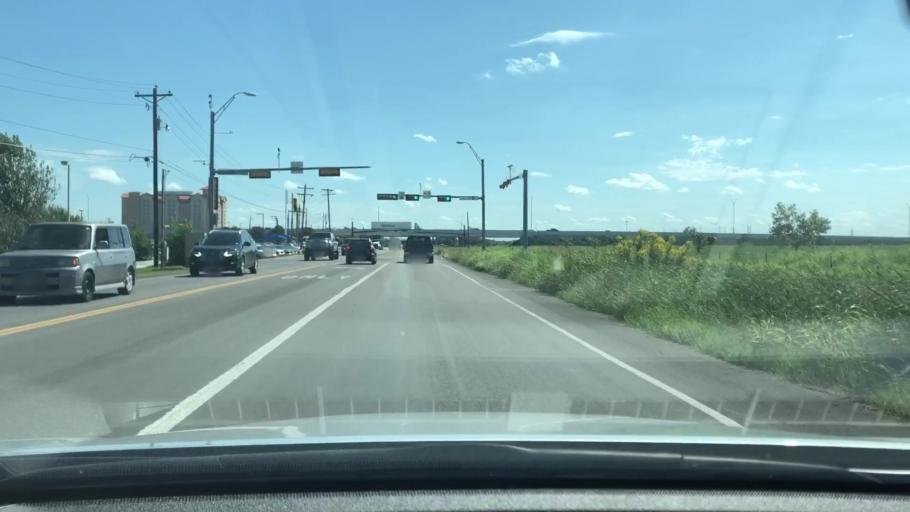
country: US
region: Texas
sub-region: Hays County
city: San Marcos
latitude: 29.8420
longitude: -97.9749
